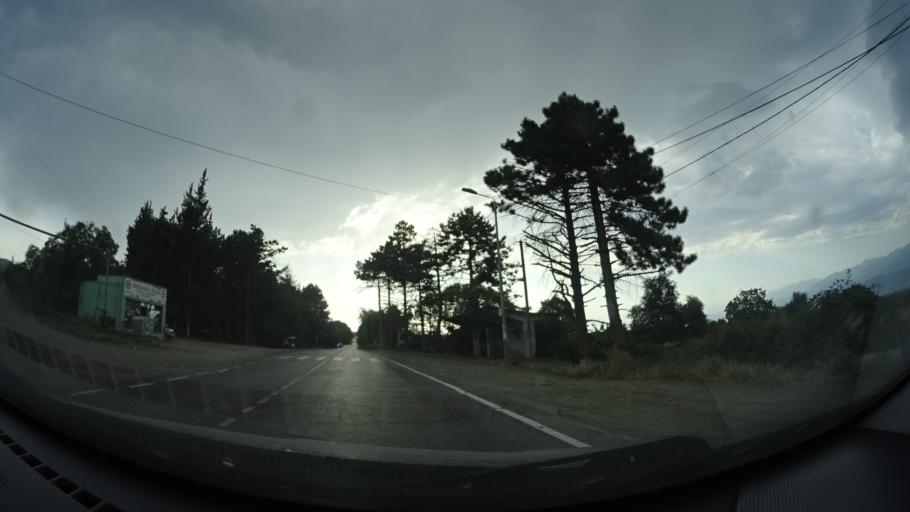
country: GE
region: Kakheti
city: Tsinandali
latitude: 41.8870
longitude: 45.5943
